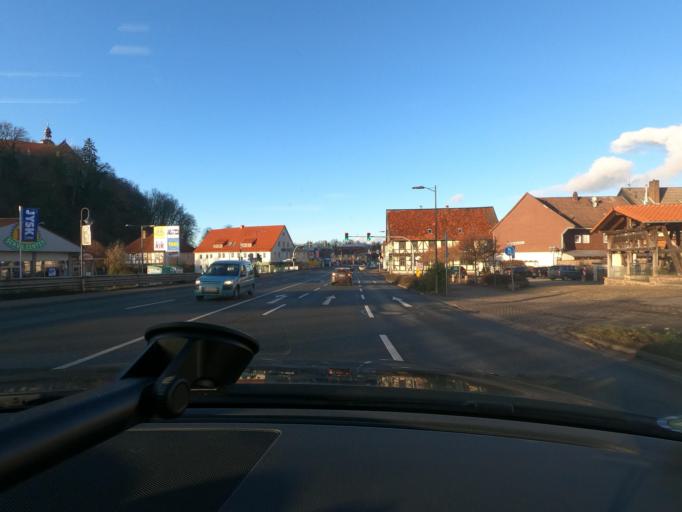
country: DE
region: Lower Saxony
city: Herzberg am Harz
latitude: 51.6546
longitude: 10.3346
